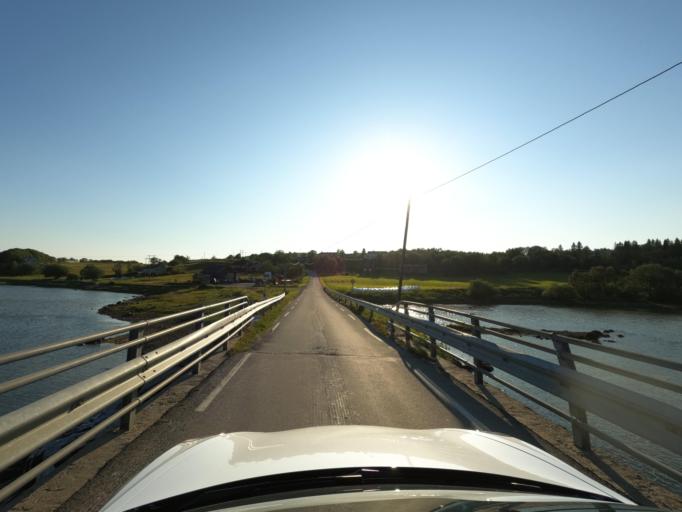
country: NO
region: Troms
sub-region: Skanland
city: Evenskjer
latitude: 68.4640
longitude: 16.6473
